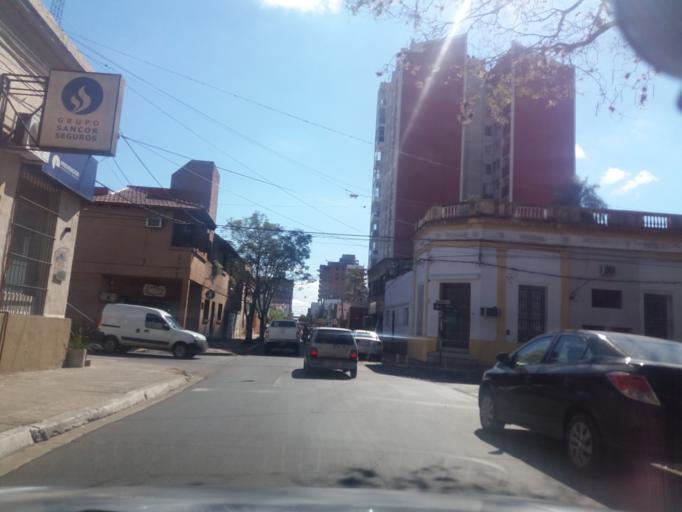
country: AR
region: Corrientes
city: Corrientes
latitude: -27.4714
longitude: -58.8335
